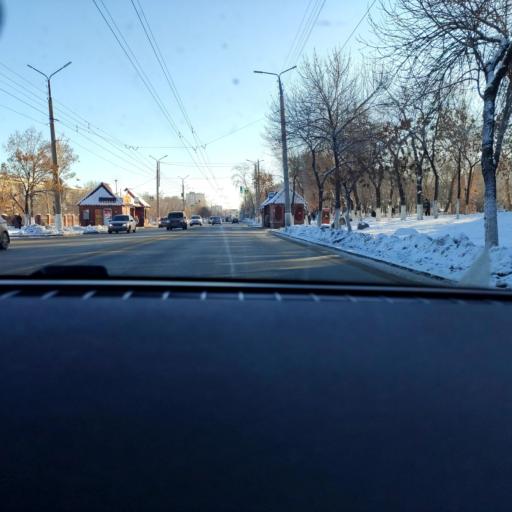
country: RU
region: Samara
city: Novokuybyshevsk
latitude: 53.0994
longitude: 49.9623
